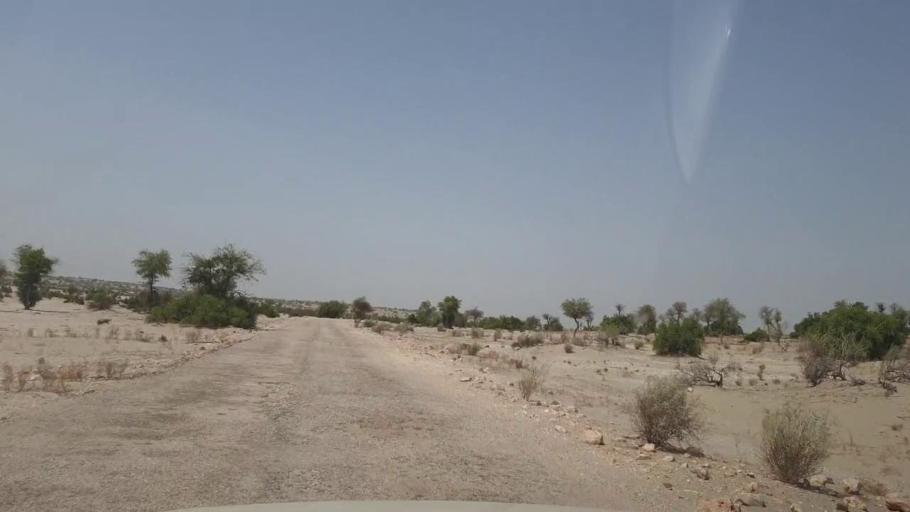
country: PK
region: Sindh
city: Khanpur
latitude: 27.3403
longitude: 69.3154
